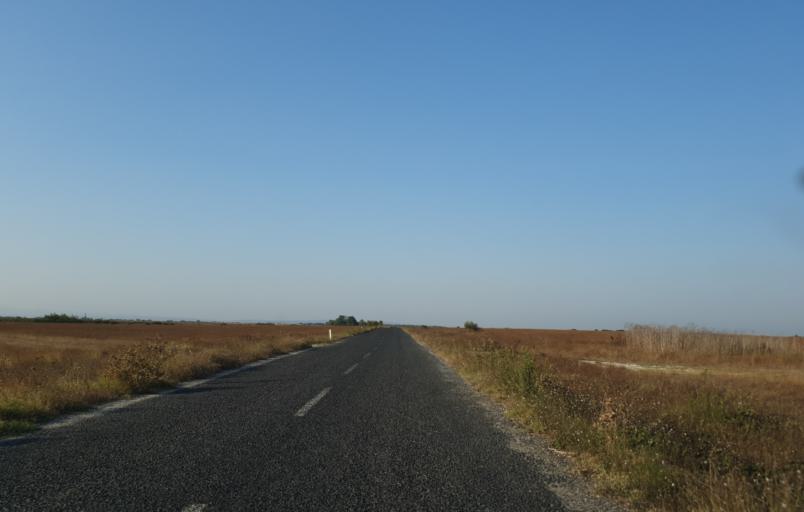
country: TR
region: Tekirdag
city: Beyazkoy
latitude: 41.4071
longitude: 27.7603
